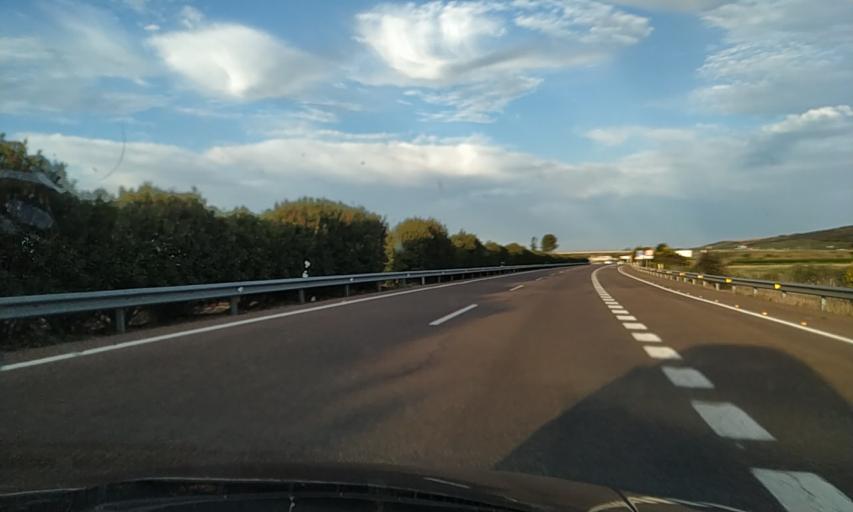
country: ES
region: Extremadura
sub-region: Provincia de Badajoz
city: Arroyo de San Servan
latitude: 38.8763
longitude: -6.4630
